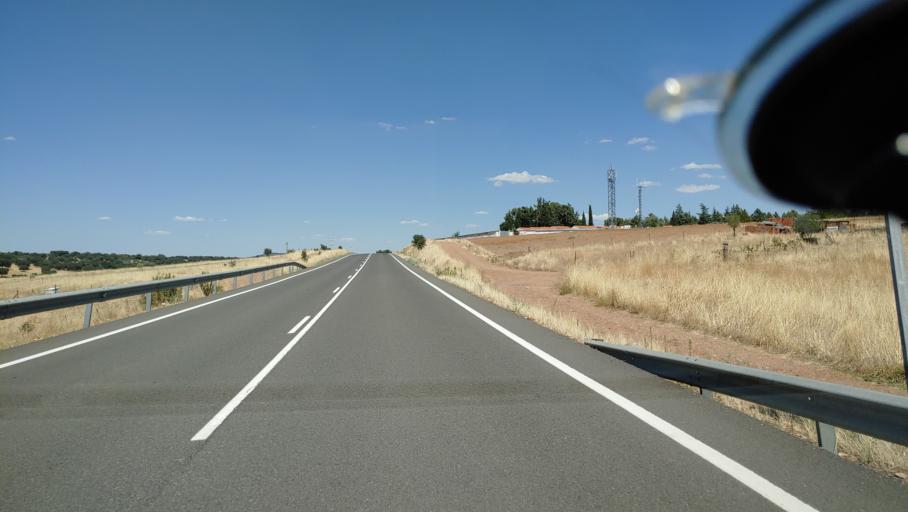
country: ES
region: Castille-La Mancha
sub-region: Provincia de Ciudad Real
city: Saceruela
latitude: 38.9456
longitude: -4.6137
